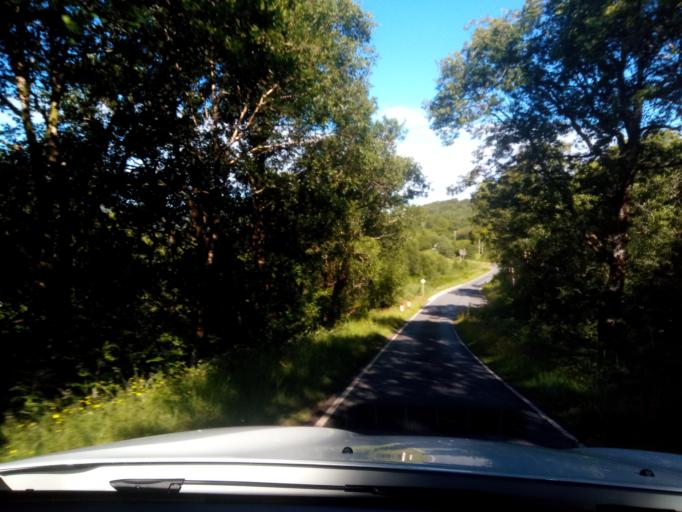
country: GB
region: Scotland
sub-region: Argyll and Bute
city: Isle Of Mull
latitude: 56.6875
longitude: -5.6603
